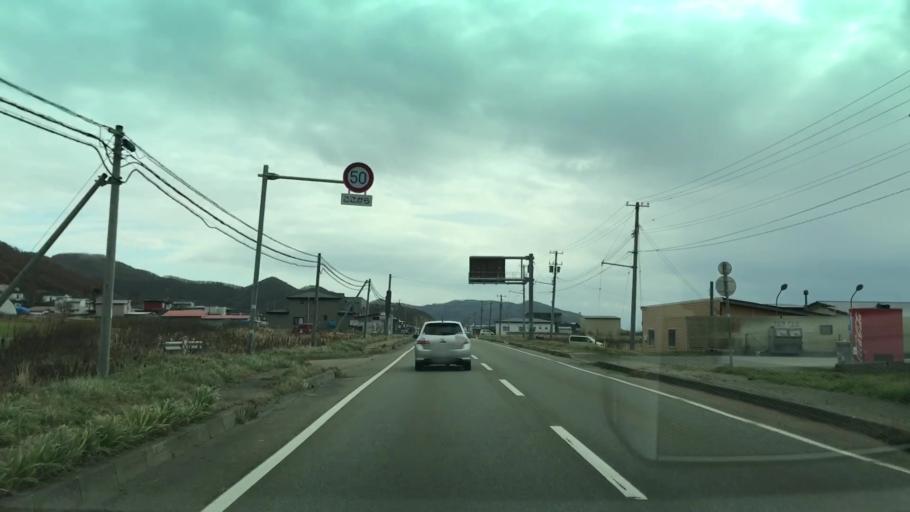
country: JP
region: Hokkaido
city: Shizunai-furukawacho
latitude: 42.0274
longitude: 143.1366
